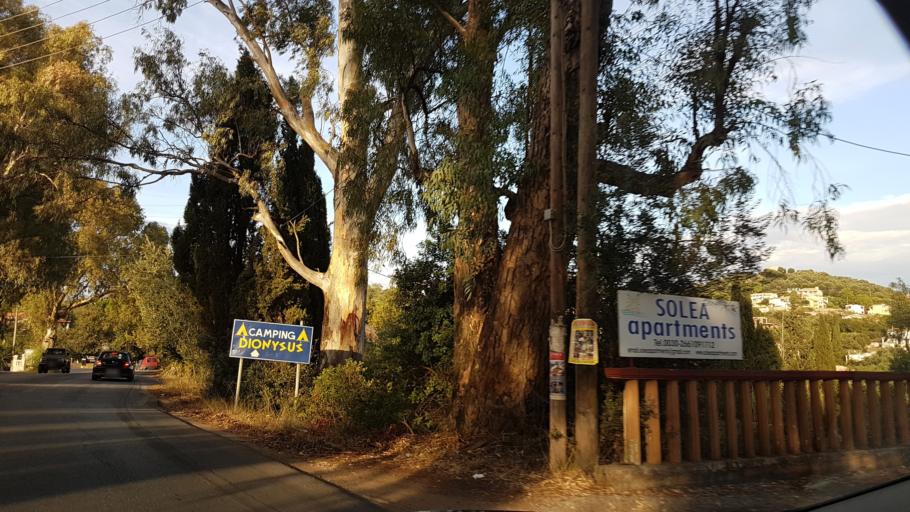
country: GR
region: Ionian Islands
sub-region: Nomos Kerkyras
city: Kontokali
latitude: 39.6629
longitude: 19.8435
